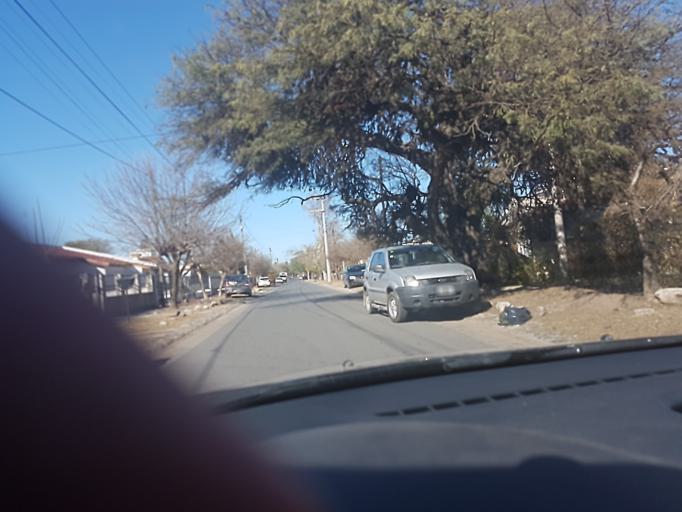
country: AR
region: Cordoba
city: Villa Allende
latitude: -31.3602
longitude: -64.2554
